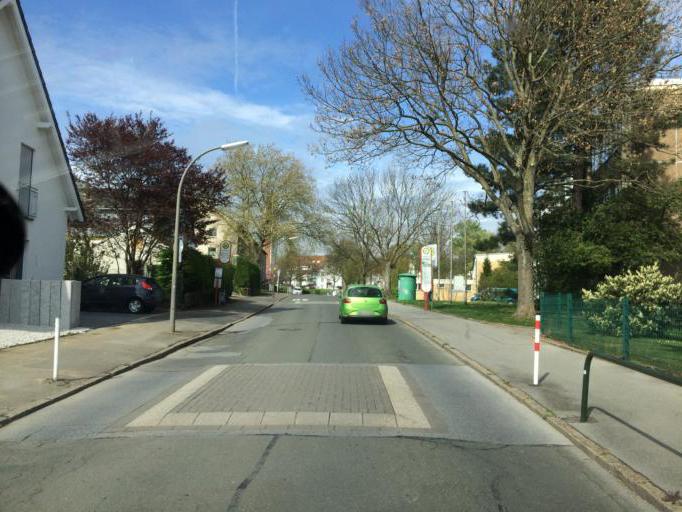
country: DE
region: North Rhine-Westphalia
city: Witten
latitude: 51.4780
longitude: 7.4092
